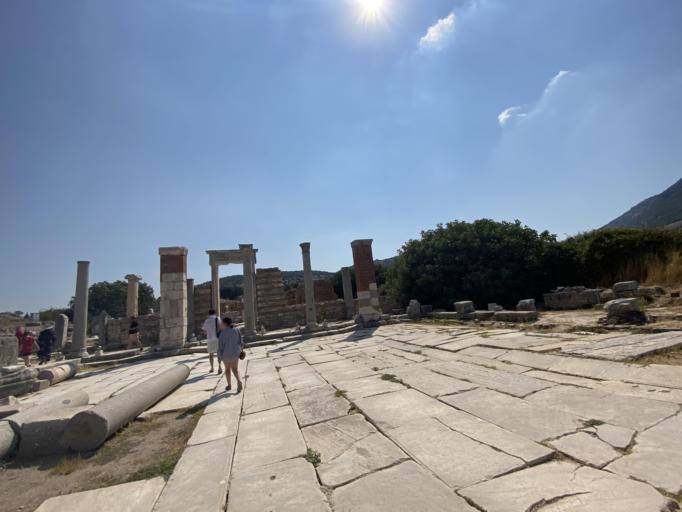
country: TR
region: Izmir
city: Selcuk
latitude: 37.9452
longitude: 27.3387
